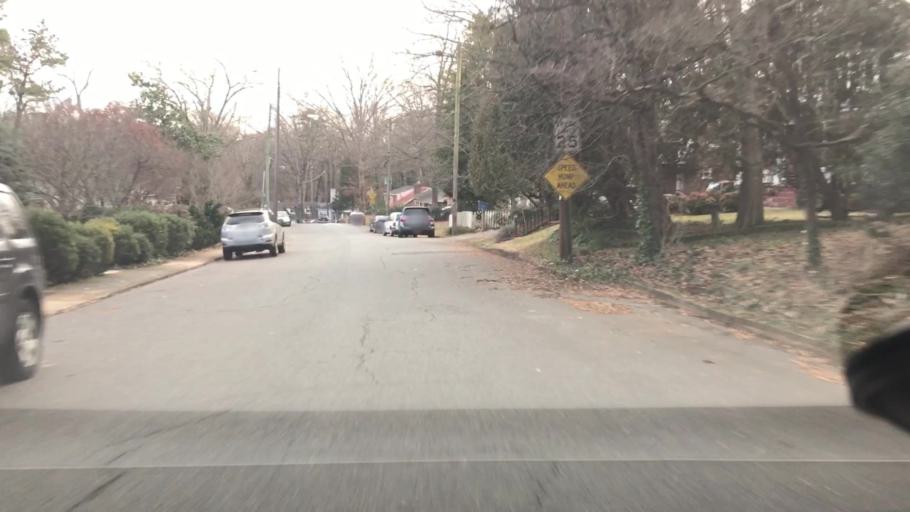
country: US
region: Virginia
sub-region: City of Charlottesville
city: Charlottesville
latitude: 38.0242
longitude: -78.5111
